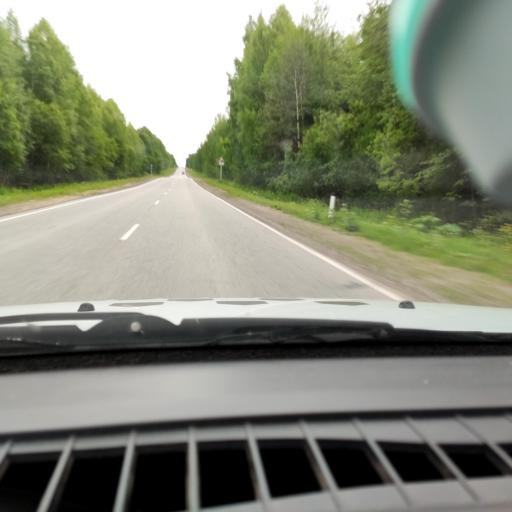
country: RU
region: Perm
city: Lys'va
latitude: 58.1483
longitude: 57.7561
